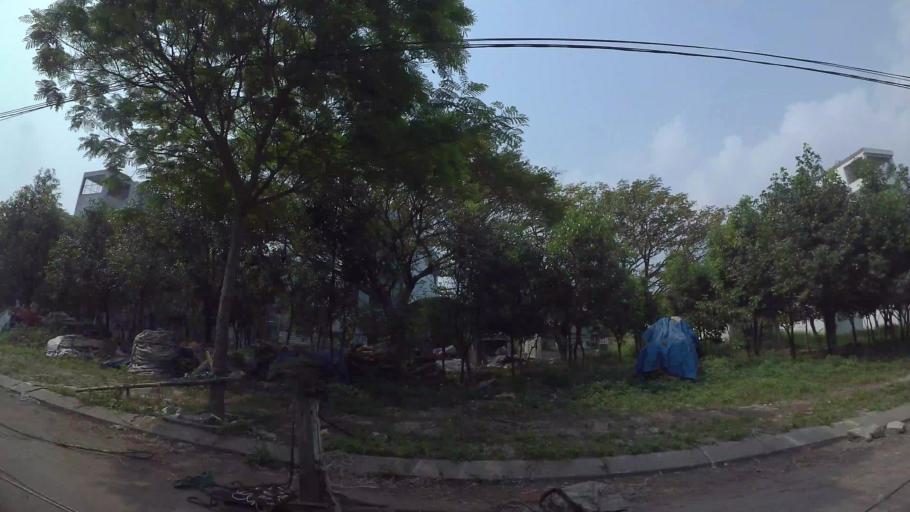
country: VN
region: Da Nang
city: Da Nang
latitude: 16.0920
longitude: 108.2388
